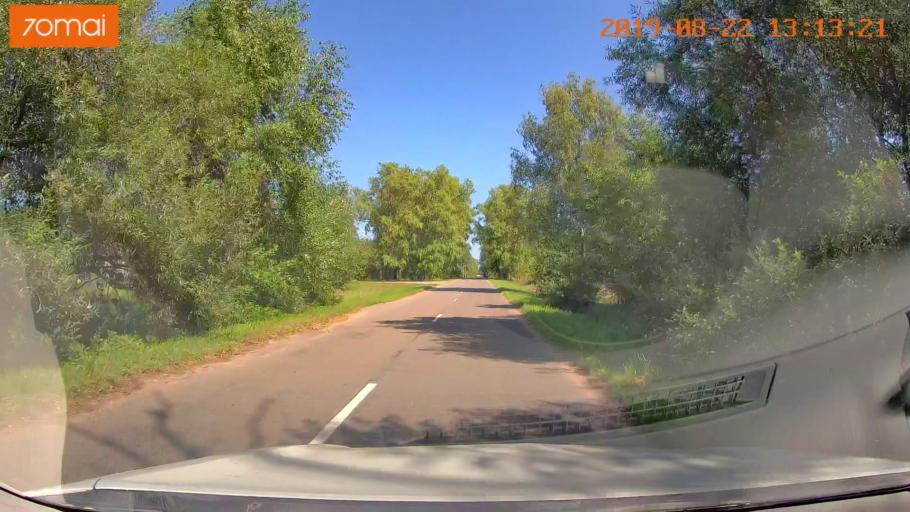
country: BY
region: Minsk
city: Prawdzinski
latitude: 53.2710
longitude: 27.8752
